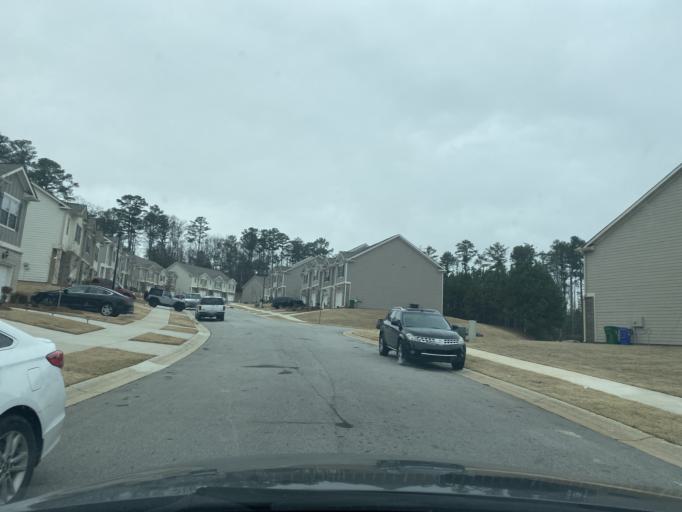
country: US
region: Georgia
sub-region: DeKalb County
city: Pine Mountain
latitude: 33.6898
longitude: -84.1548
